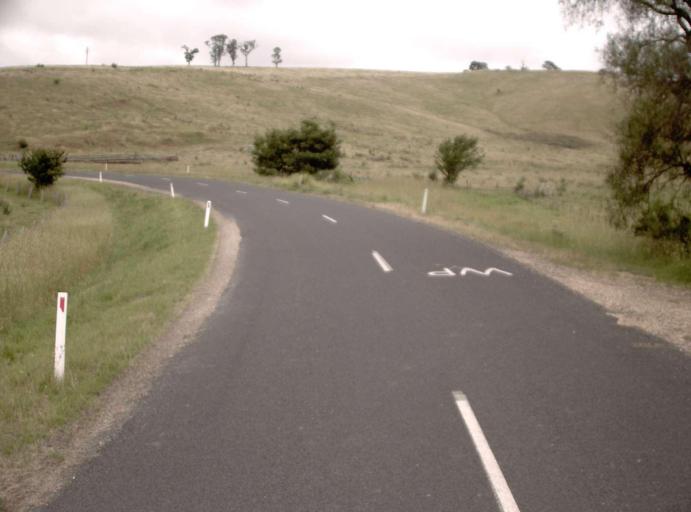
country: AU
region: Victoria
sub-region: Wellington
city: Heyfield
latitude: -37.8873
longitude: 146.7250
